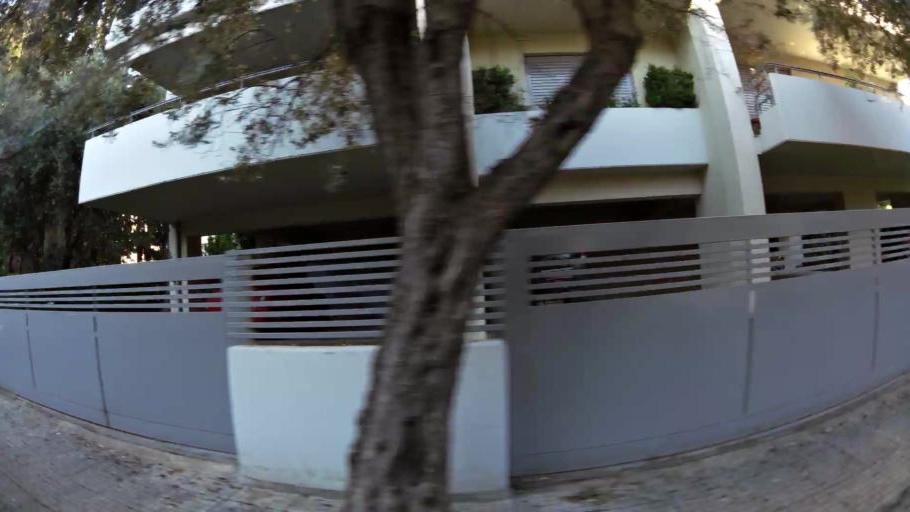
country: GR
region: Attica
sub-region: Nomarchia Athinas
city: Cholargos
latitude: 38.0077
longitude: 23.7963
